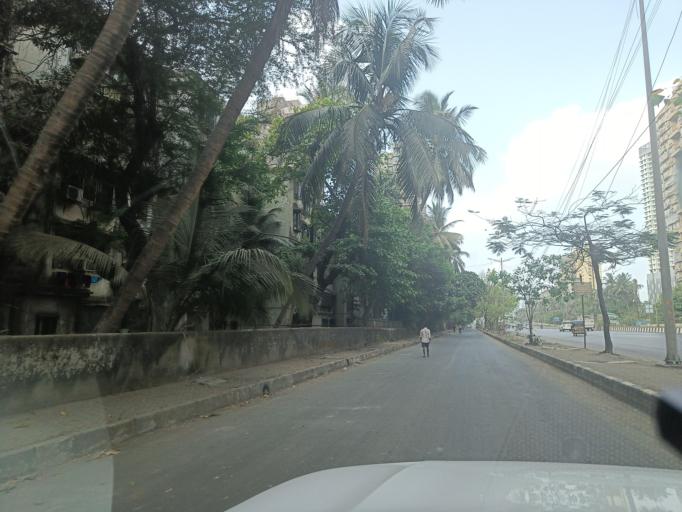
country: IN
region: Maharashtra
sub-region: Mumbai Suburban
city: Powai
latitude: 19.1152
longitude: 72.9351
